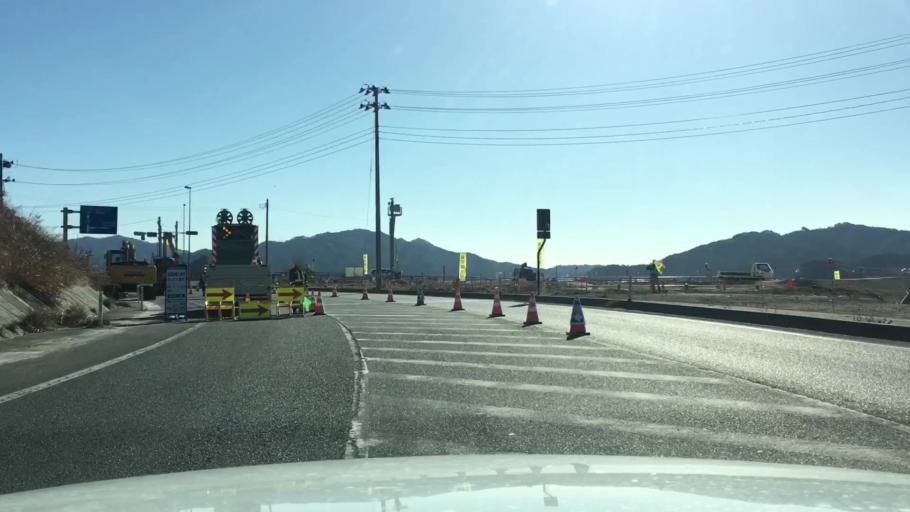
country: JP
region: Iwate
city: Yamada
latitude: 39.4767
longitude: 141.9564
